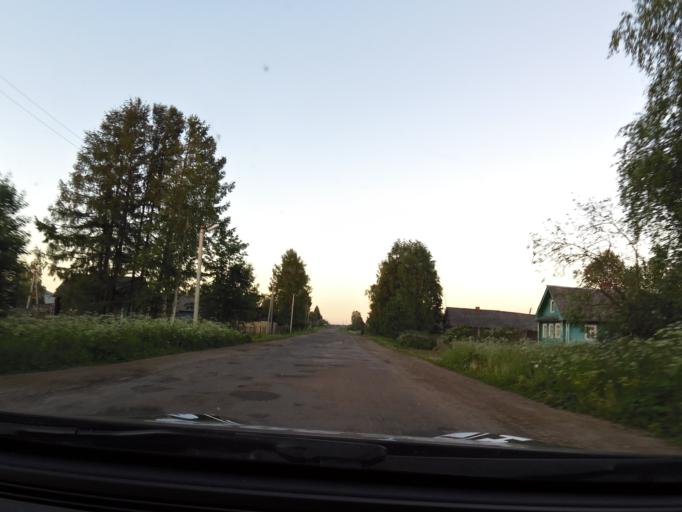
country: RU
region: Leningrad
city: Voznesen'ye
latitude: 60.8499
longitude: 35.5672
